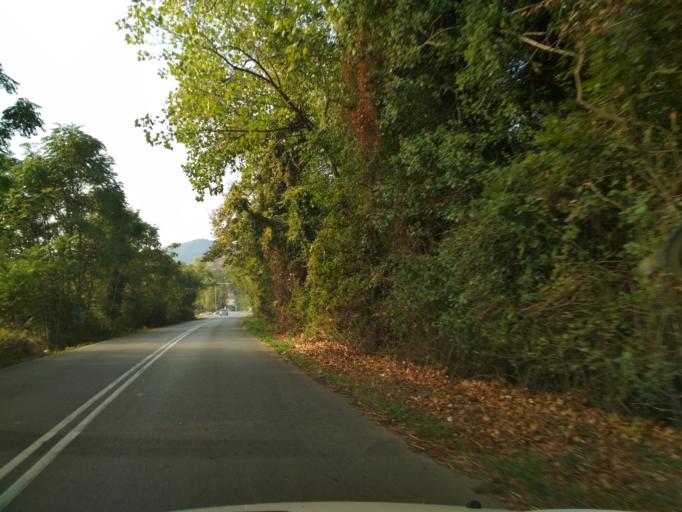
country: GR
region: Central Greece
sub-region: Nomos Evvoias
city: Prokopion
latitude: 38.7381
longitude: 23.4926
